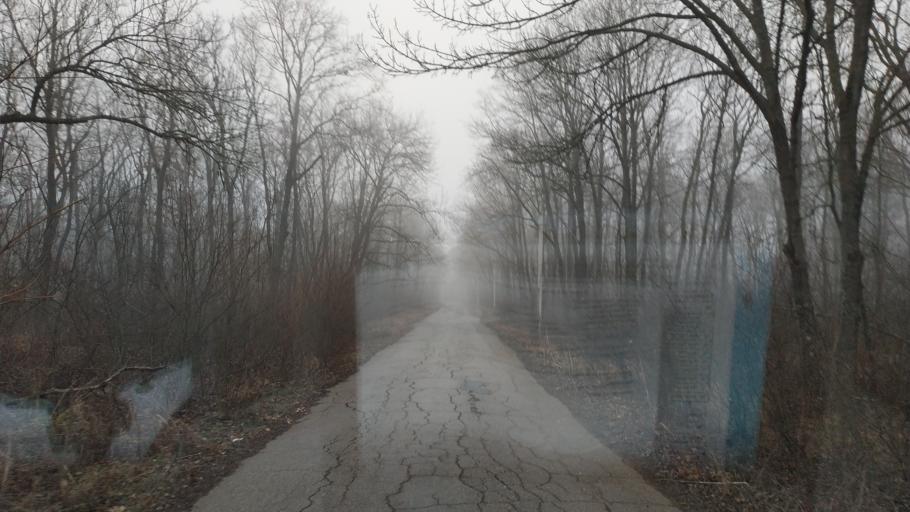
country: MD
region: Laloveni
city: Ialoveni
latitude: 46.9465
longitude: 28.7012
